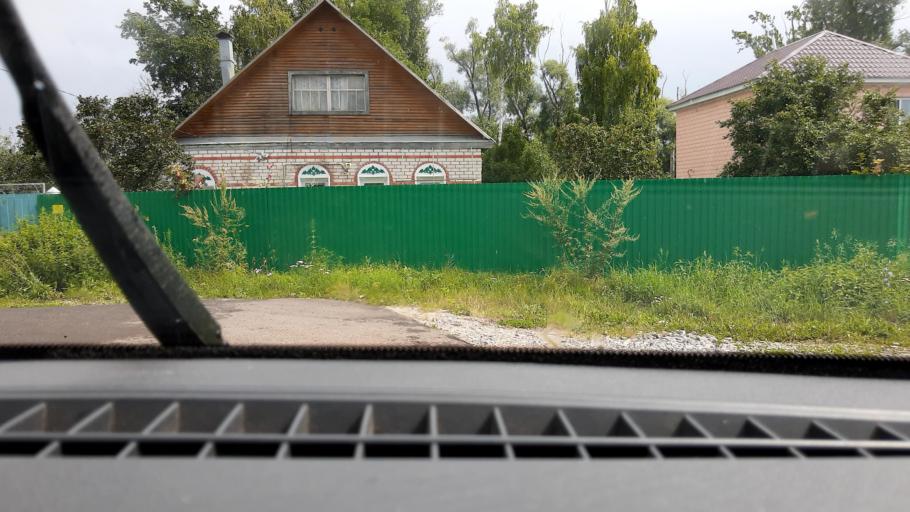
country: RU
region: Bashkortostan
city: Mikhaylovka
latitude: 54.8076
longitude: 55.8965
